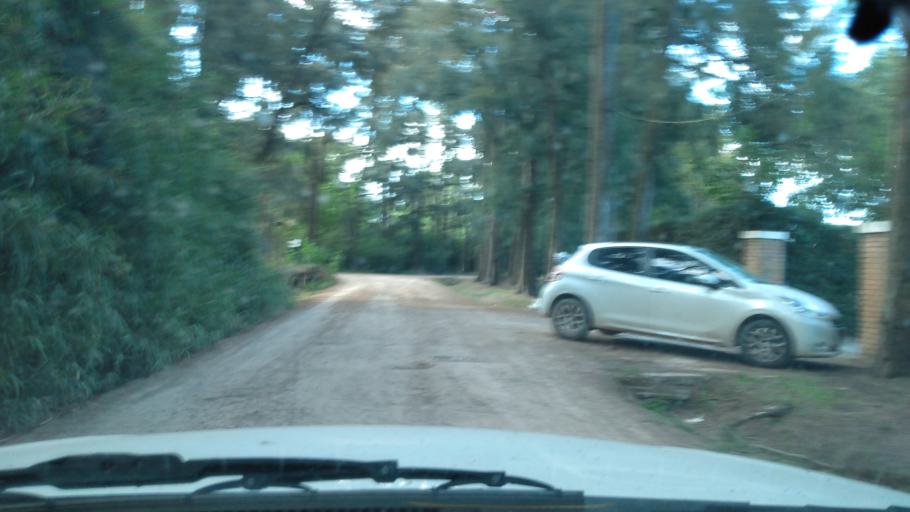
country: AR
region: Buenos Aires
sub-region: Partido de Lujan
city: Lujan
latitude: -34.5496
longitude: -59.1608
